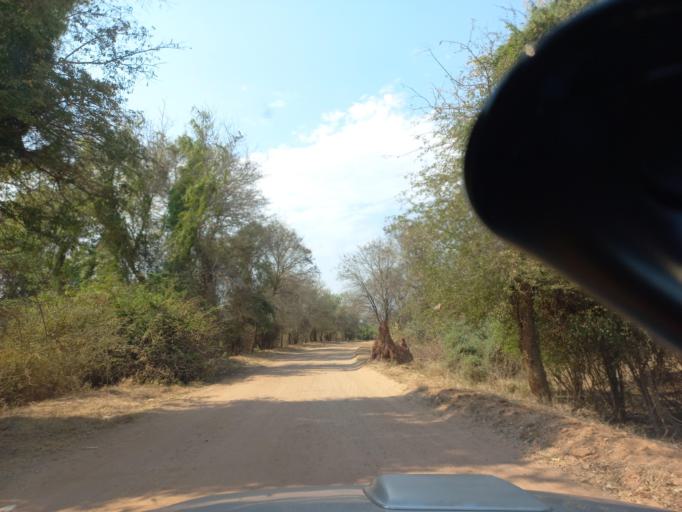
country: ZW
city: Chirundu
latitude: -15.9293
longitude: 28.8717
